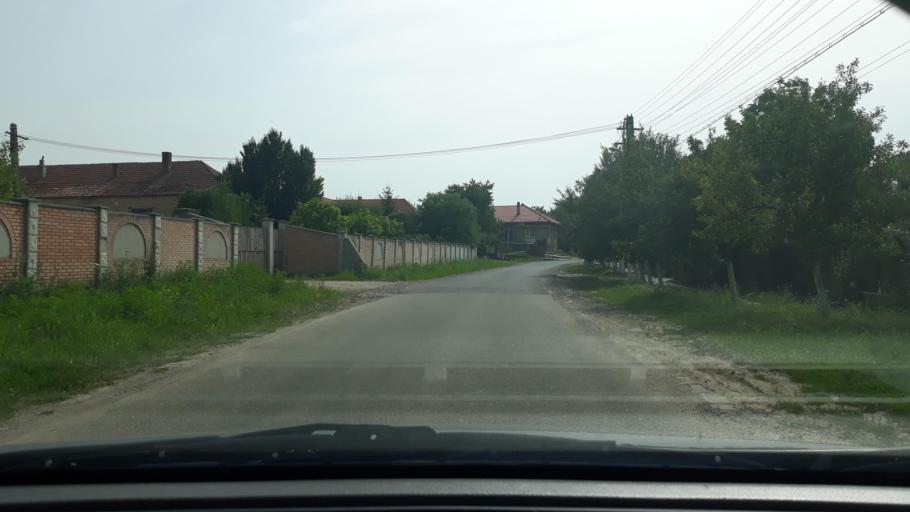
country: RO
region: Bihor
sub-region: Comuna Tauteu
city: Tauteu
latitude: 47.2687
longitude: 22.3349
